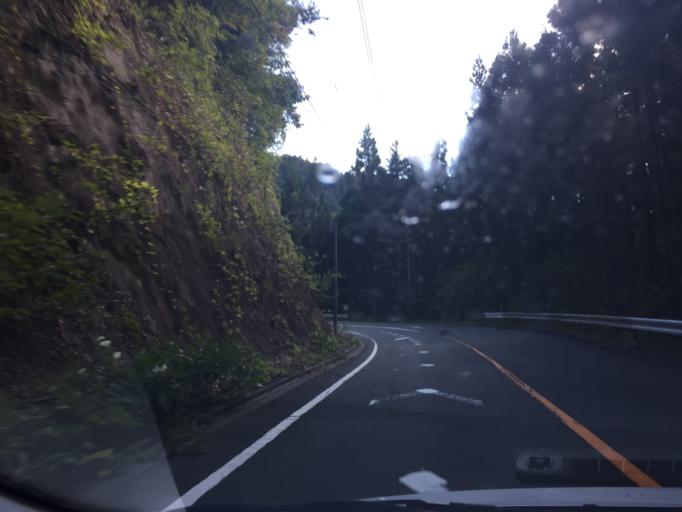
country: JP
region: Aichi
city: Shinshiro
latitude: 35.1239
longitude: 137.6734
